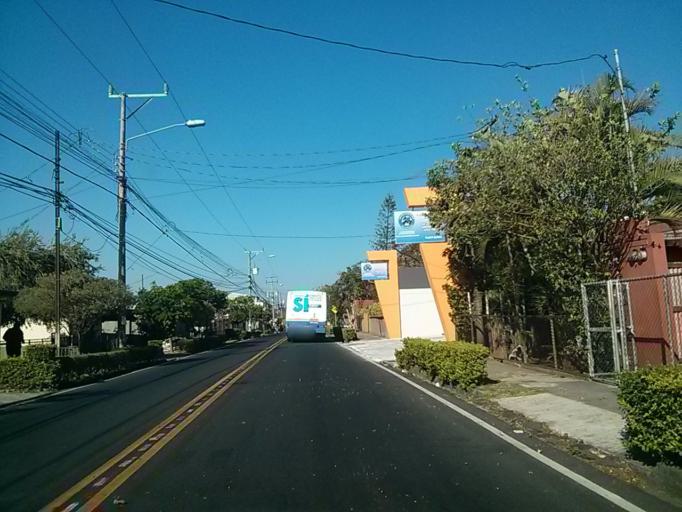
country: CR
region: Heredia
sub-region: Canton de Belen
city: San Antonio
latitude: 9.9820
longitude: -84.1911
